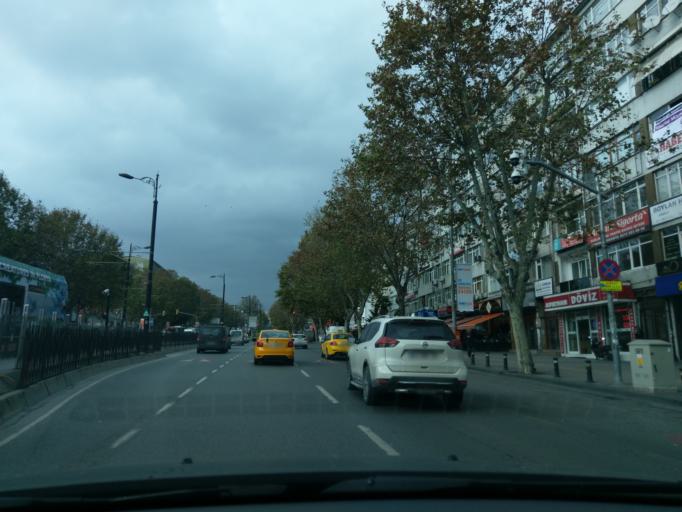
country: TR
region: Istanbul
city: Istanbul
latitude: 41.0102
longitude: 28.9466
